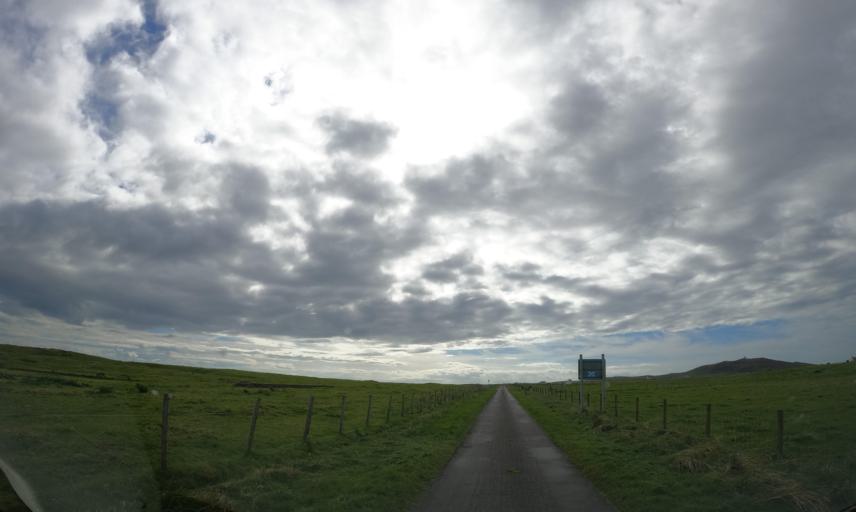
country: GB
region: Scotland
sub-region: Eilean Siar
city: Barra
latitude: 56.4830
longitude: -6.9011
